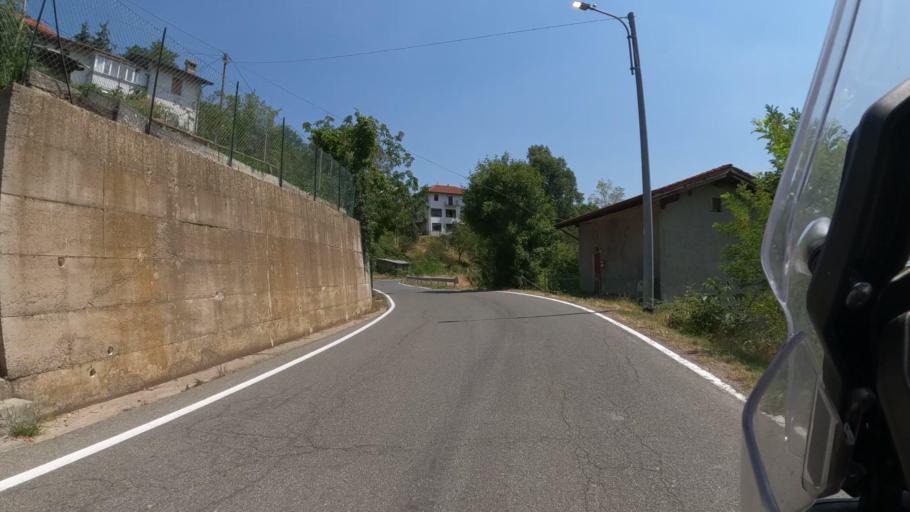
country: IT
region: Piedmont
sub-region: Provincia di Alessandria
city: Cassinelle-Concentrico
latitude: 44.5790
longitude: 8.5520
